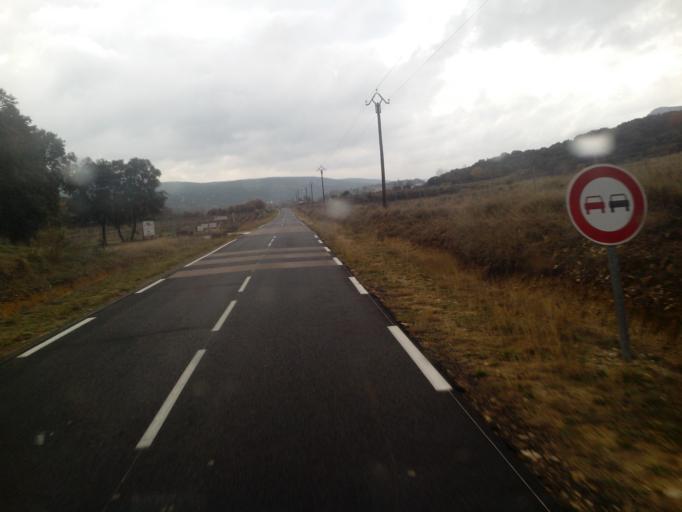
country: FR
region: Languedoc-Roussillon
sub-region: Departement du Gard
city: Saint-Hippolyte-du-Fort
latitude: 43.9388
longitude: 3.8024
